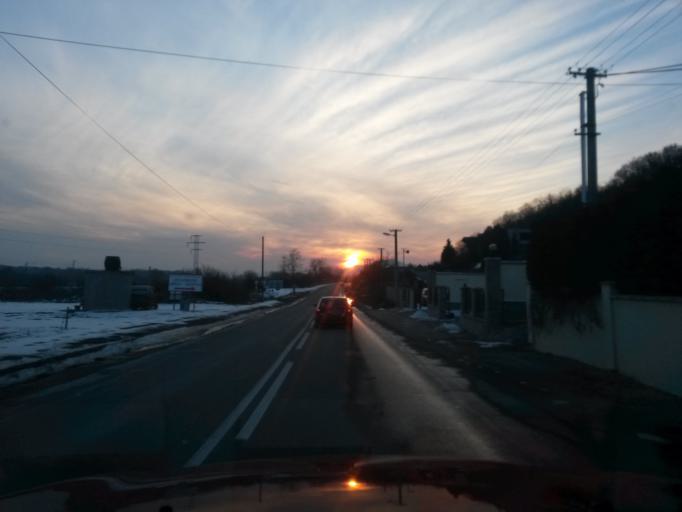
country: HU
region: Borsod-Abauj-Zemplen
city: Karcsa
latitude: 48.3590
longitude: 21.8070
